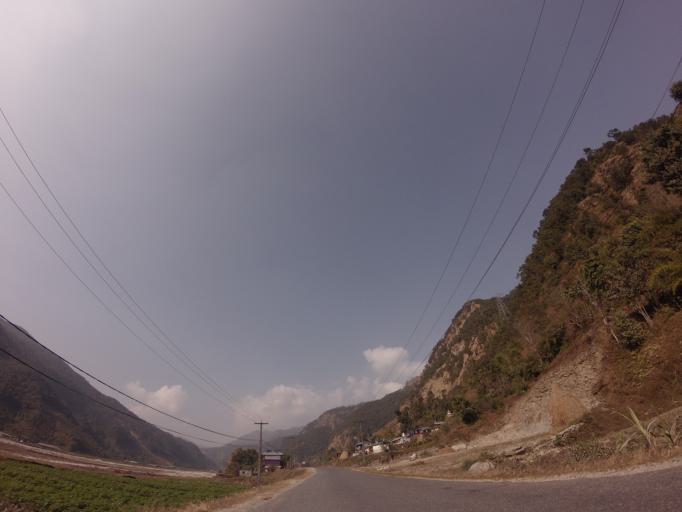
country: NP
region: Western Region
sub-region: Gandaki Zone
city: Pokhara
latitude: 28.2880
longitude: 83.8971
